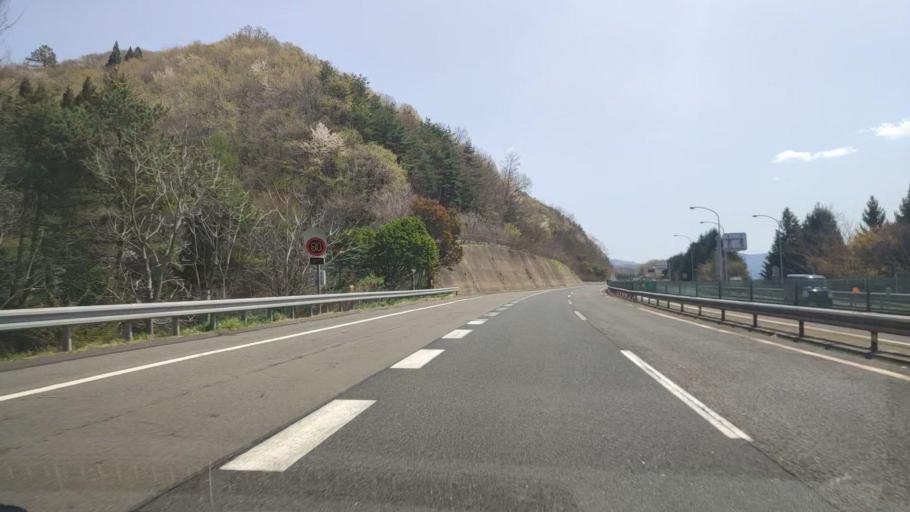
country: JP
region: Iwate
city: Ichinohe
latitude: 40.2326
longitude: 141.3001
